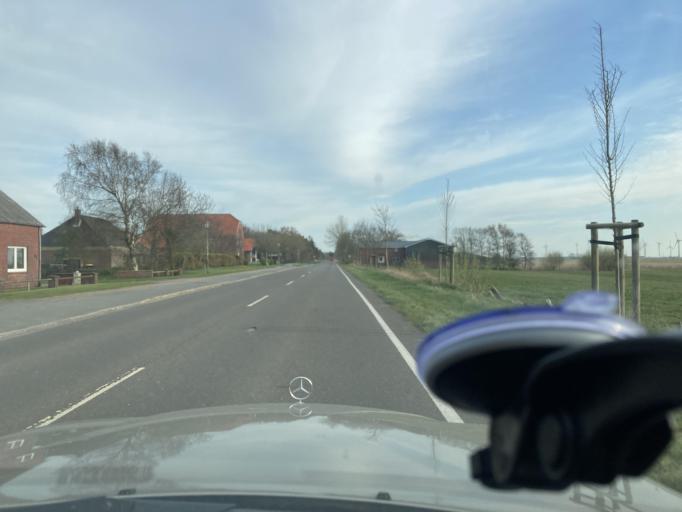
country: DE
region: Schleswig-Holstein
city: Krempel
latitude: 54.2957
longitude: 9.0400
